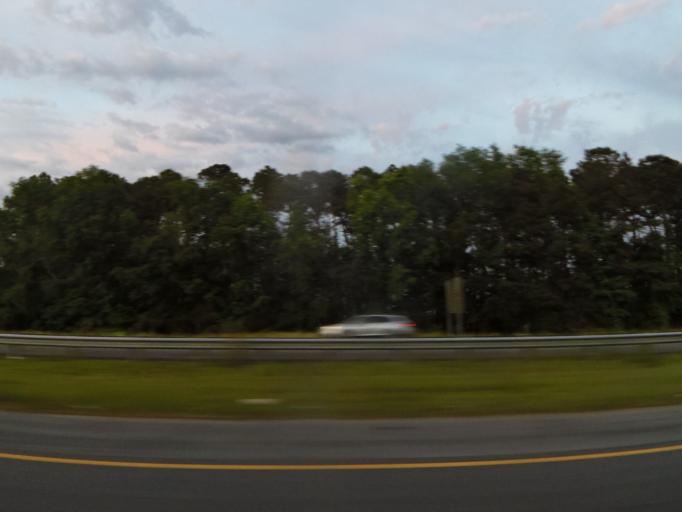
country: US
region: Georgia
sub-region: Bryan County
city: Richmond Hill
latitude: 31.9418
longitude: -81.3357
